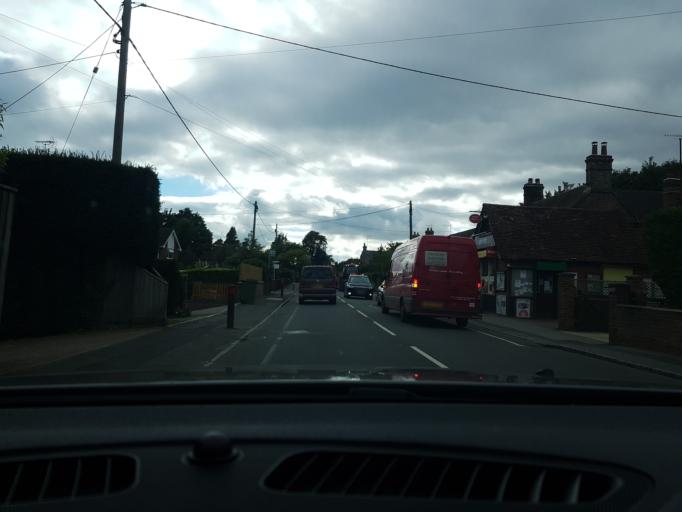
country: GB
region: England
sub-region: West Berkshire
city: Hermitage
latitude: 51.4544
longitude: -1.2701
